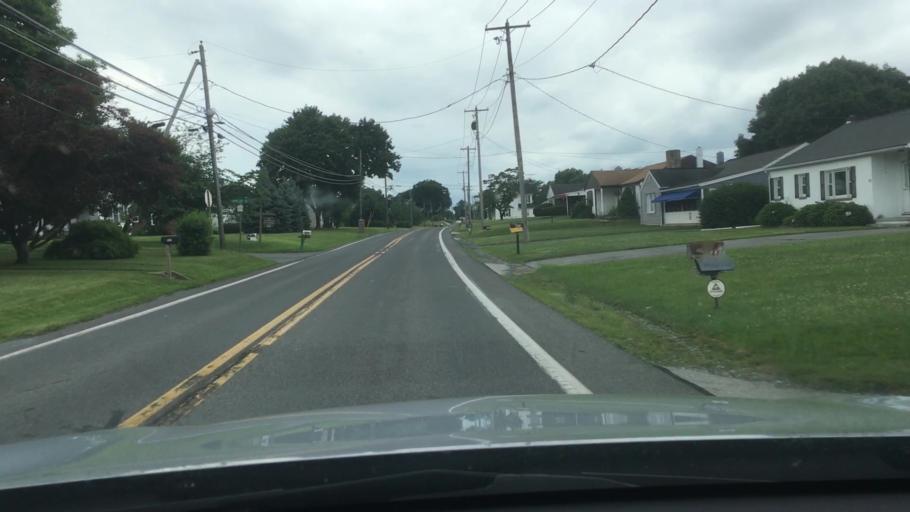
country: US
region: Pennsylvania
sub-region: Franklin County
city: Chambersburg
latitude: 39.9230
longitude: -77.6989
